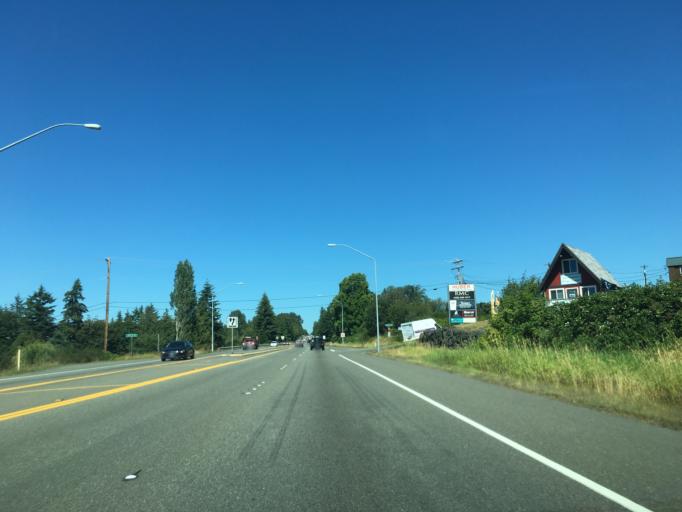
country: US
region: Washington
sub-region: Snohomish County
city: West Lake Stevens
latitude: 47.9868
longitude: -122.1335
